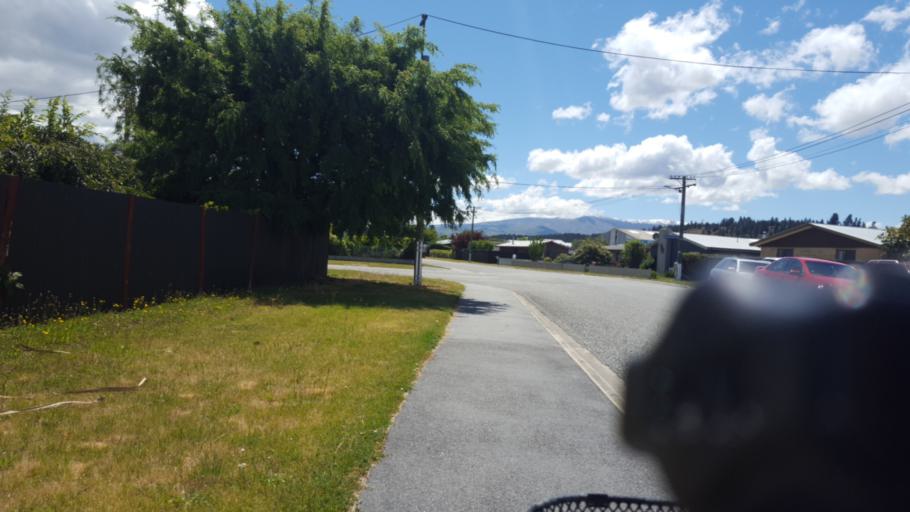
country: NZ
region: Otago
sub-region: Queenstown-Lakes District
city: Wanaka
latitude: -45.2466
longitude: 169.3920
